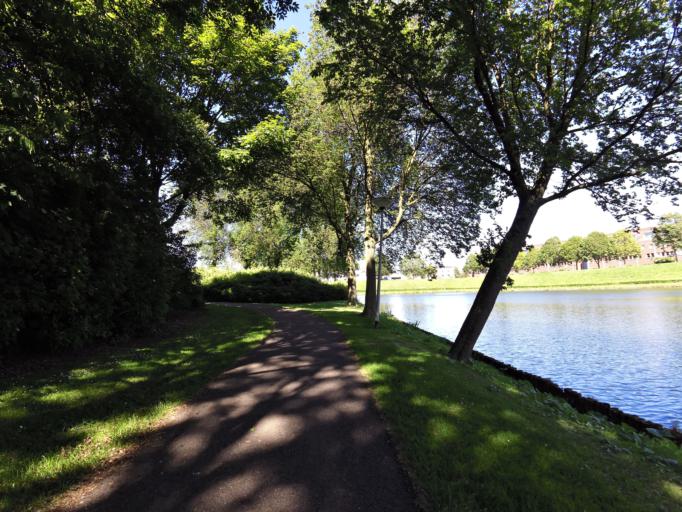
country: NL
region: South Holland
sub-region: Gemeente Hellevoetsluis
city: Hellevoetsluis
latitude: 51.8277
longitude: 4.1261
